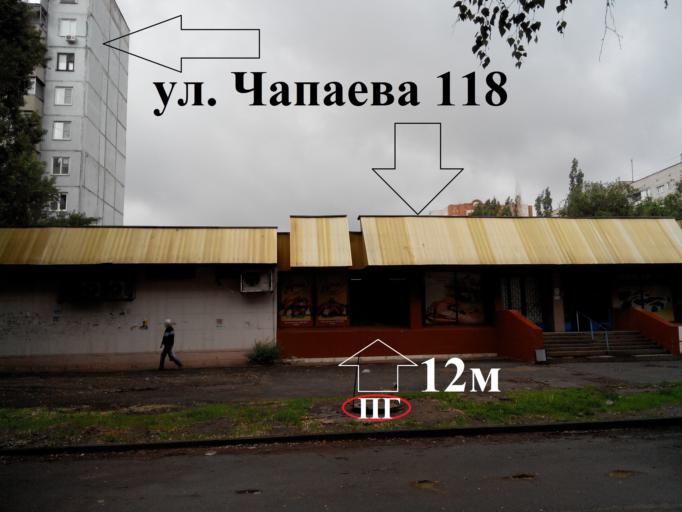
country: RU
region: Voronezj
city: Voronezh
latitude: 51.6370
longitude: 39.1864
